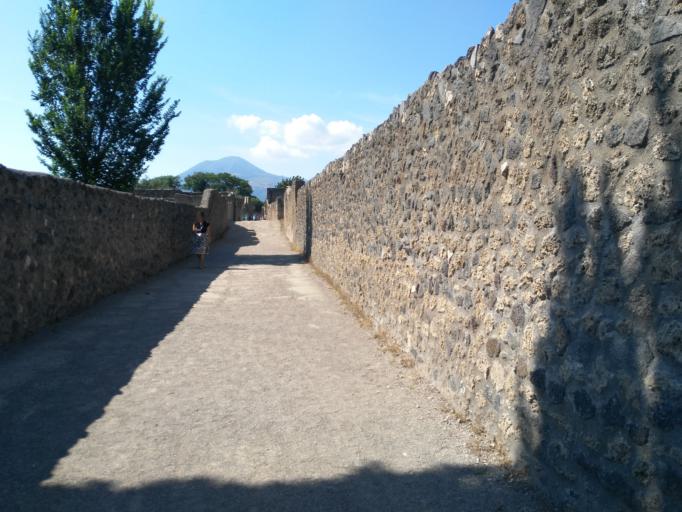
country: IT
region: Campania
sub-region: Provincia di Napoli
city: Pompei
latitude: 40.7493
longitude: 14.4925
